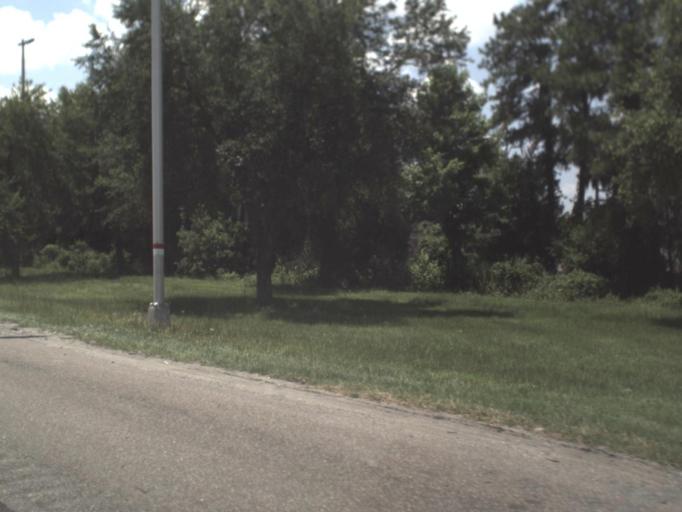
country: US
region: Florida
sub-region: Duval County
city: Jacksonville
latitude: 30.3974
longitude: -81.5626
